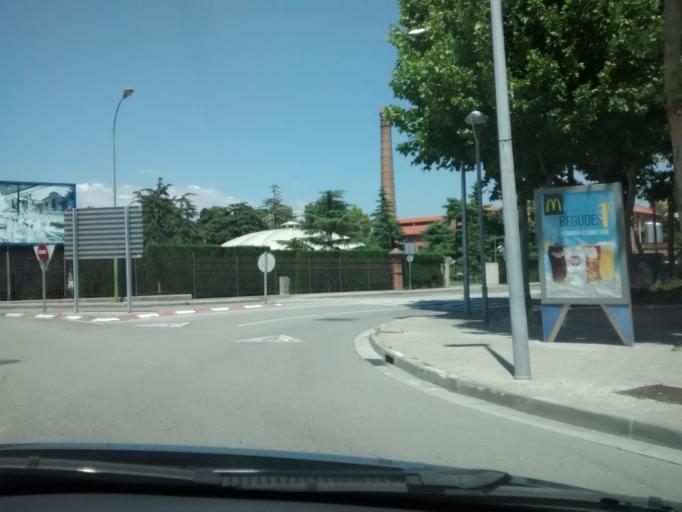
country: ES
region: Catalonia
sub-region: Provincia de Barcelona
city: Sant Joan Despi
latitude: 41.3548
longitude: 2.0635
